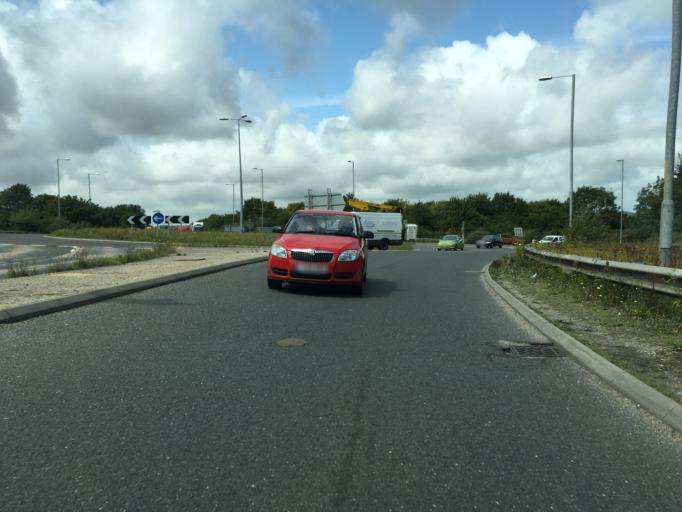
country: GB
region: England
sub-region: East Sussex
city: Lewes
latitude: 50.8646
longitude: 0.0256
